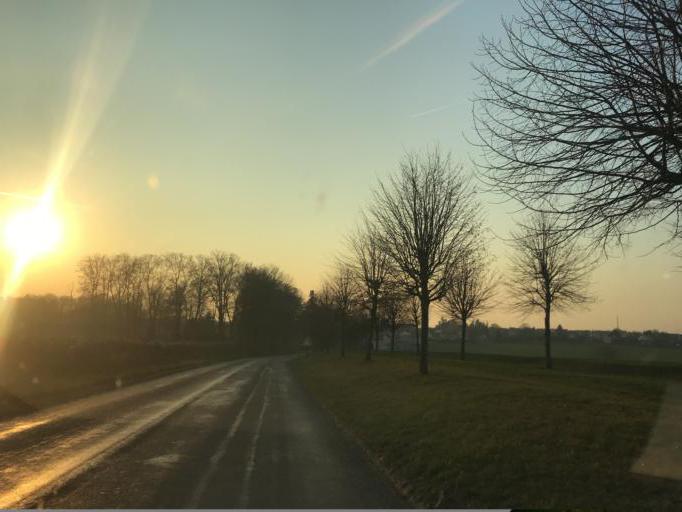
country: FR
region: Ile-de-France
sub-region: Departement de Seine-et-Marne
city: Juilly
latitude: 49.0151
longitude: 2.7148
